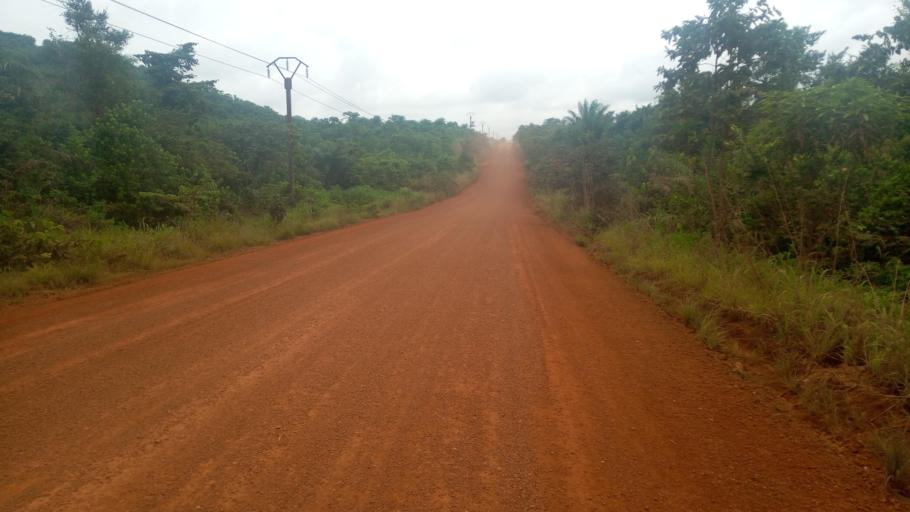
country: SL
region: Southern Province
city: Mogbwemo
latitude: 7.7103
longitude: -12.2849
